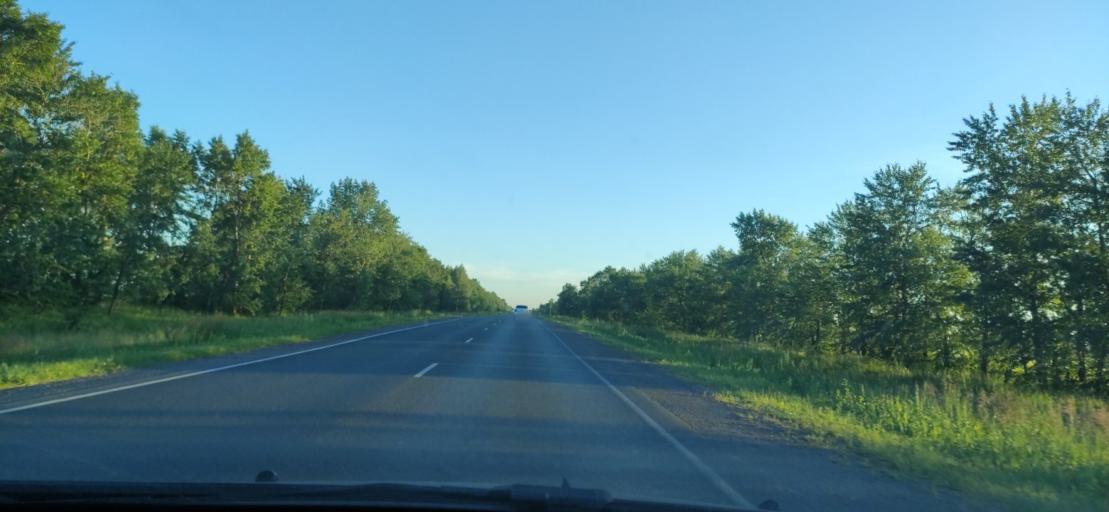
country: RU
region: Ulyanovsk
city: Cherdakly
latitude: 54.4099
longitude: 48.8767
